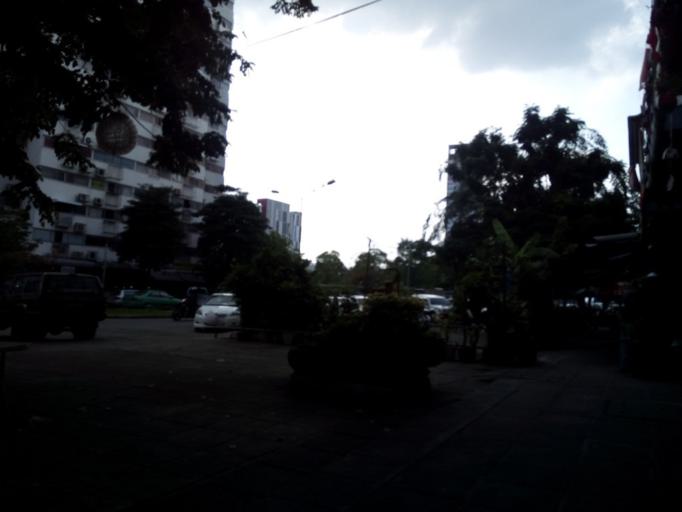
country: TH
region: Bangkok
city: Don Mueang
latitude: 13.9172
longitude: 100.5556
